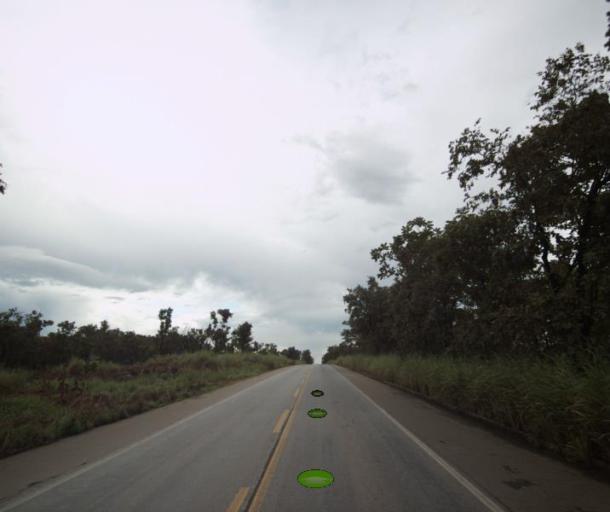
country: BR
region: Goias
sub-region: Porangatu
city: Porangatu
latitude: -13.6371
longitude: -49.0411
